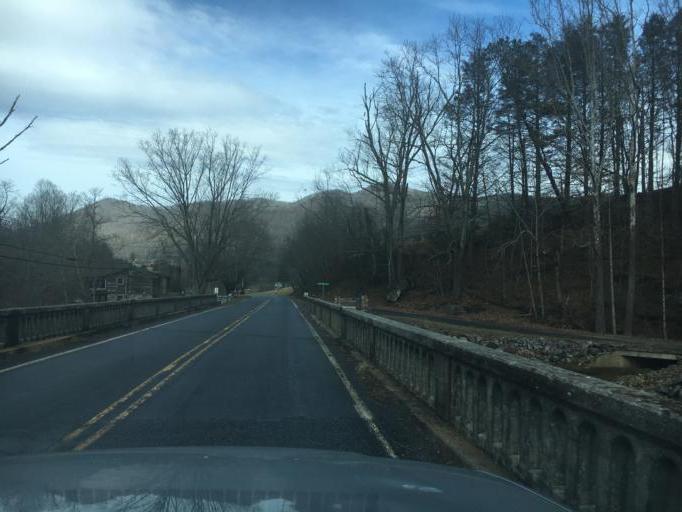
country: US
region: North Carolina
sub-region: Haywood County
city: Canton
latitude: 35.4384
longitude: -82.8138
